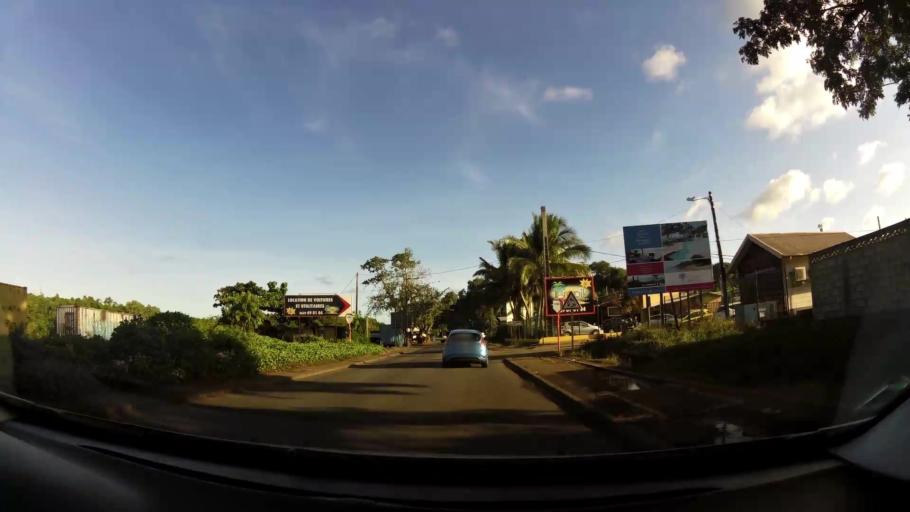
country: YT
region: Mamoudzou
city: Mamoudzou
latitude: -12.7954
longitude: 45.2161
